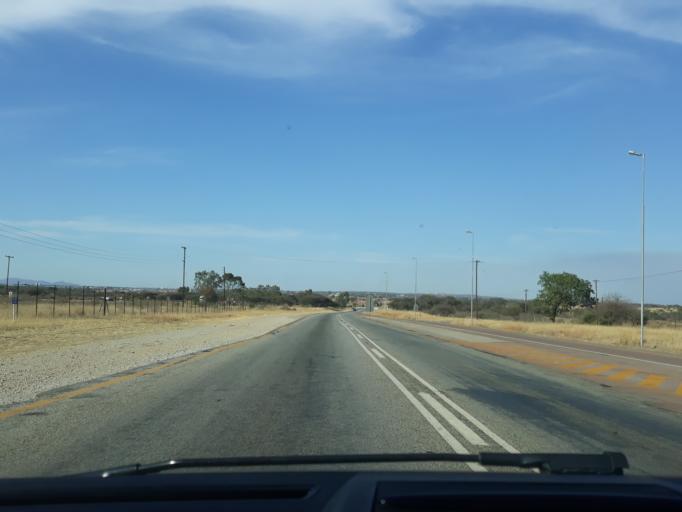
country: ZA
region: Limpopo
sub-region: Capricorn District Municipality
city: Polokwane
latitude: -23.9520
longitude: 29.3985
